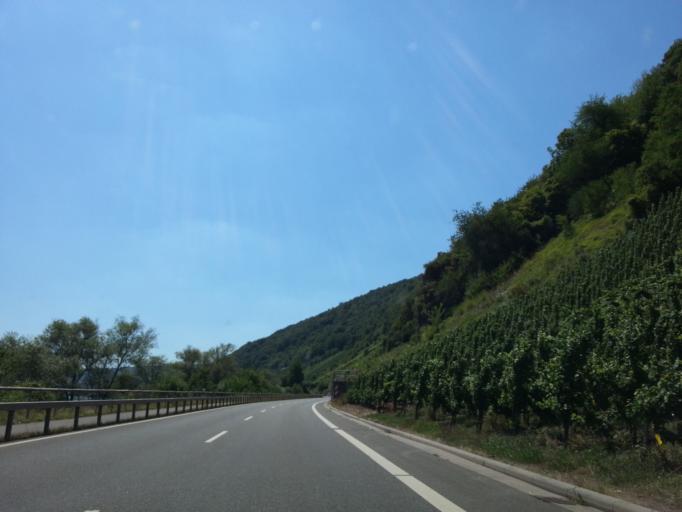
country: DE
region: Rheinland-Pfalz
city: Neumagen-Dhron
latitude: 49.8554
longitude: 6.8904
